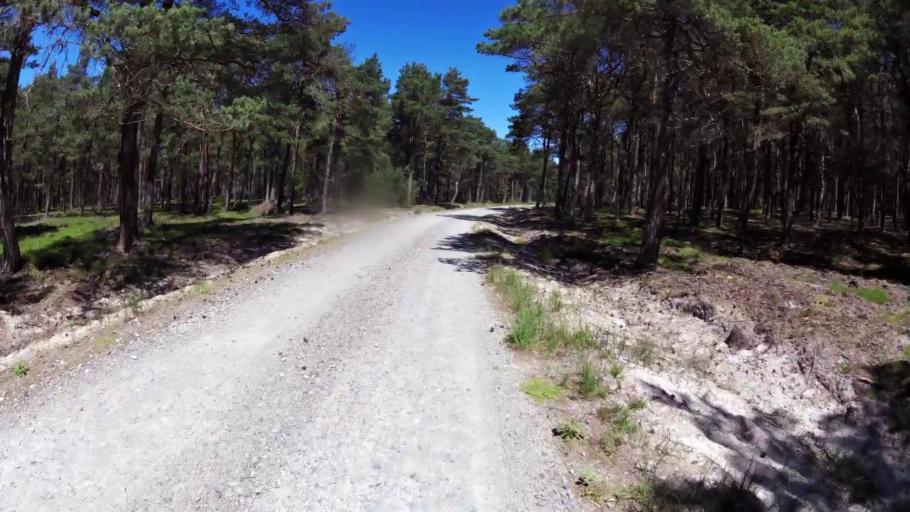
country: PL
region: West Pomeranian Voivodeship
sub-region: Powiat gryficki
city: Trzebiatow
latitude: 54.1124
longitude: 15.1965
